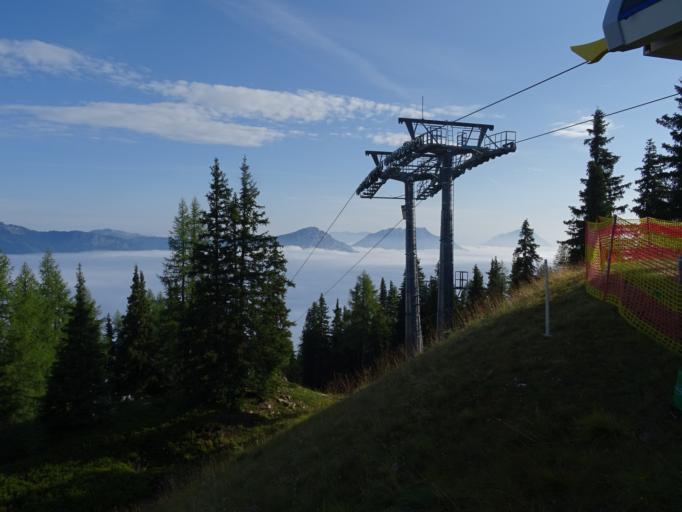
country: AT
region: Styria
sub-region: Politischer Bezirk Liezen
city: Haus
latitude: 47.3789
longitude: 13.7692
